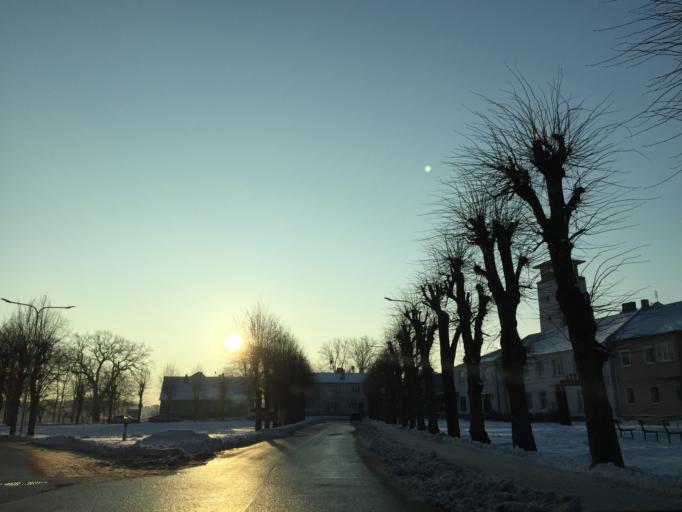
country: LV
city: Tireli
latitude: 56.9431
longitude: 23.6190
